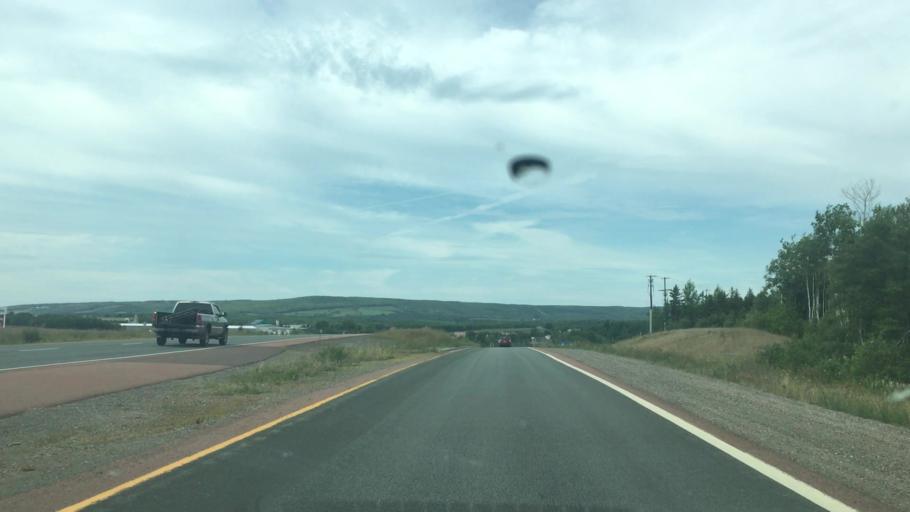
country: CA
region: Nova Scotia
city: Antigonish
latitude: 45.6111
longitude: -61.9943
